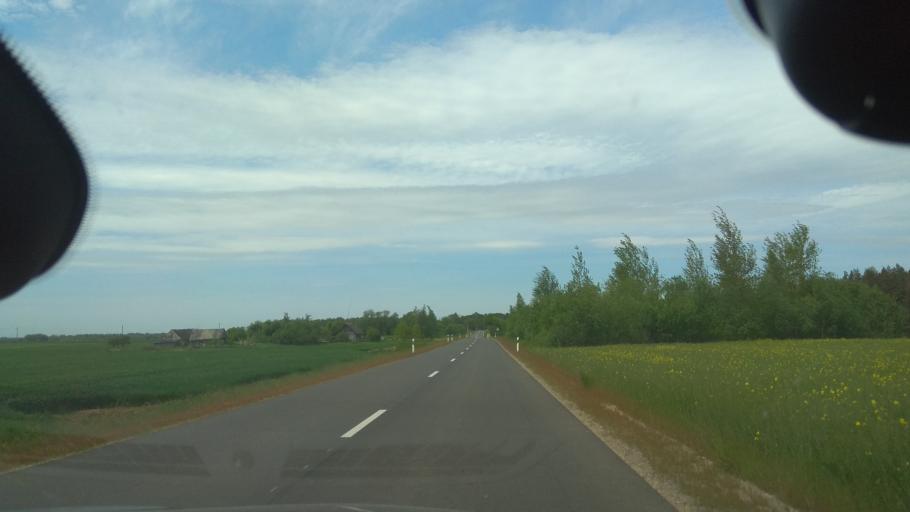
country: LT
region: Vilnius County
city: Ukmerge
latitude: 55.1156
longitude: 24.6373
